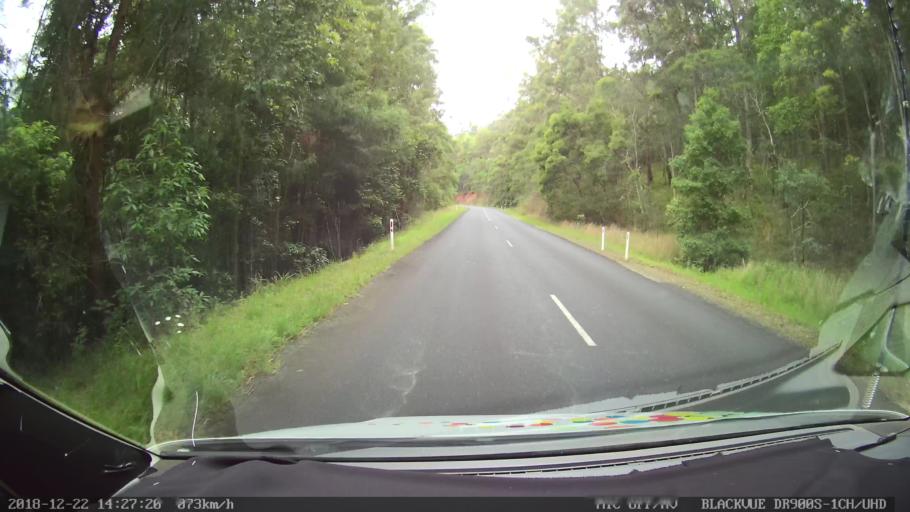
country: AU
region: New South Wales
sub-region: Bellingen
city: Dorrigo
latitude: -30.0643
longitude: 152.6344
